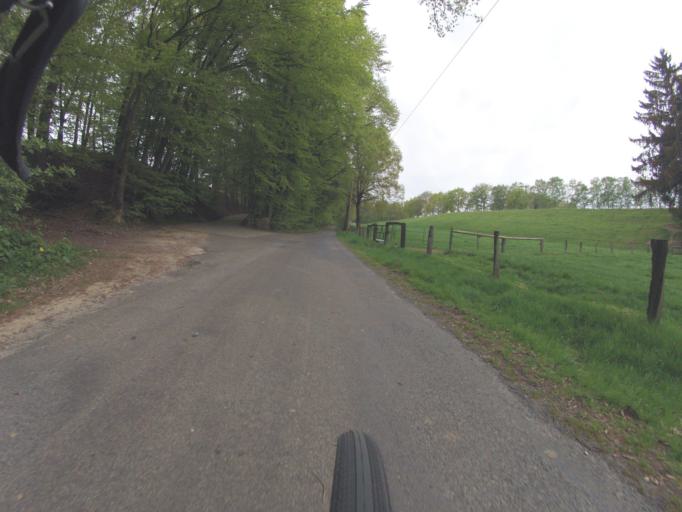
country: DE
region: North Rhine-Westphalia
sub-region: Regierungsbezirk Munster
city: Mettingen
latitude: 52.3036
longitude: 7.7960
